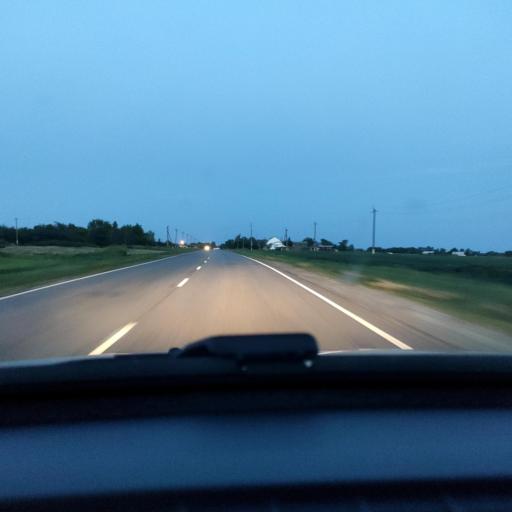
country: RU
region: Voronezj
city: Verkhnyaya Khava
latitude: 51.6850
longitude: 39.9353
